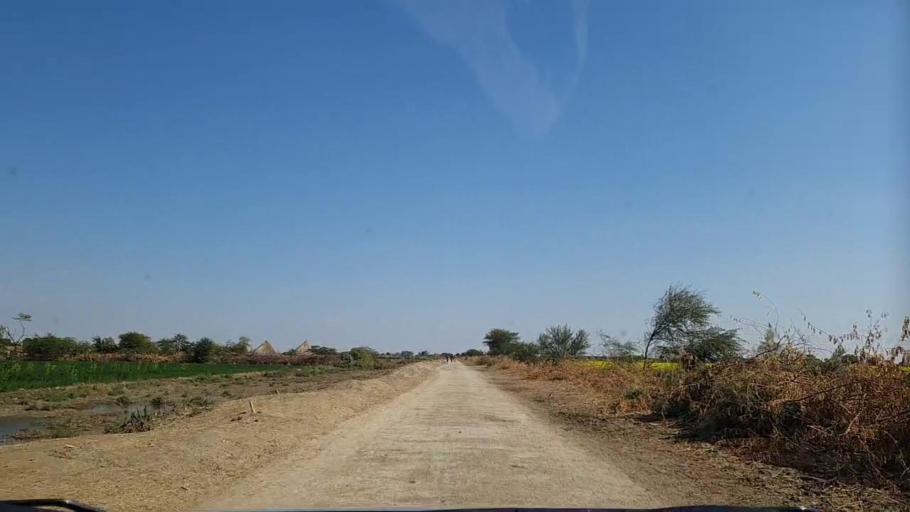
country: PK
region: Sindh
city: Pithoro
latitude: 25.6863
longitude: 69.4731
